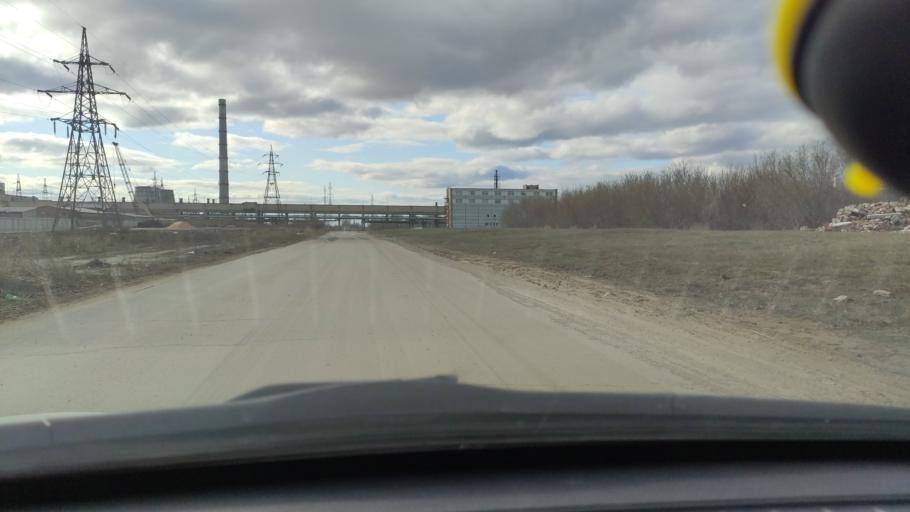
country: RU
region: Samara
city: Tol'yatti
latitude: 53.5488
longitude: 49.4621
